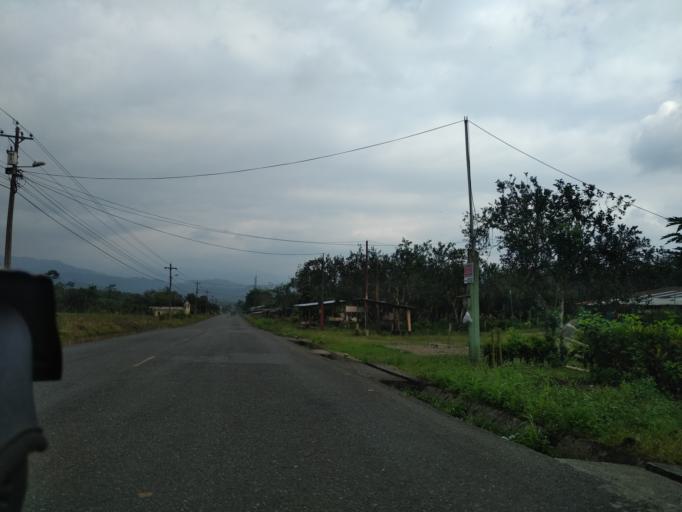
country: EC
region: Cotopaxi
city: La Mana
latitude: -0.8941
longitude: -79.1617
